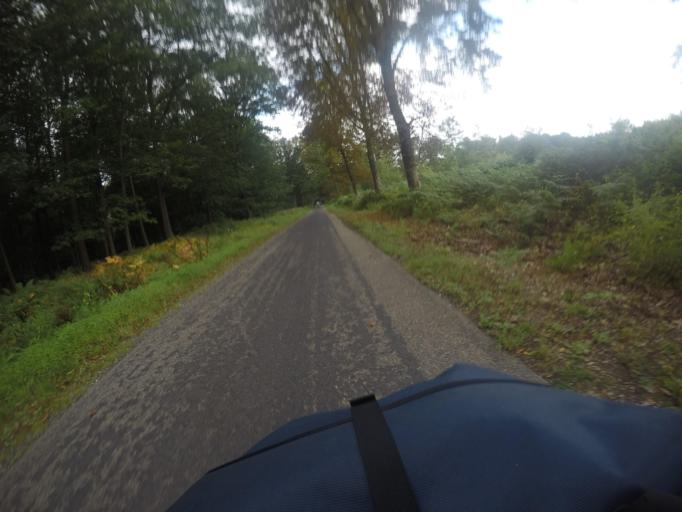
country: NL
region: Gelderland
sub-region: Gemeente Groesbeek
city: De Horst
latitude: 51.7428
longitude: 5.9876
